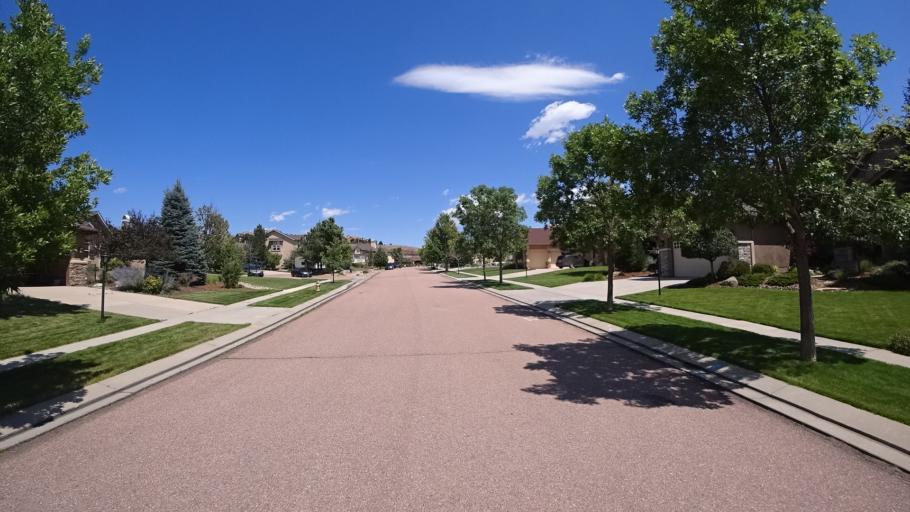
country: US
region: Colorado
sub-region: El Paso County
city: Black Forest
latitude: 38.9707
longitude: -104.7708
